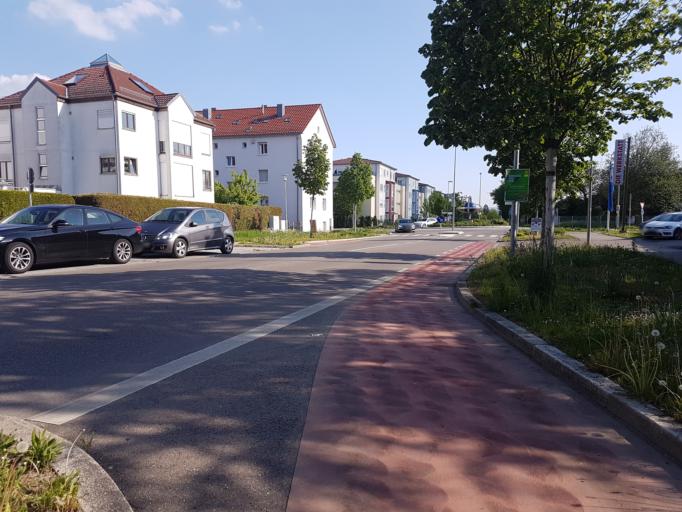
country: DE
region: Baden-Wuerttemberg
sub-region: Regierungsbezirk Stuttgart
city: Kornwestheim
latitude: 48.8554
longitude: 9.1848
